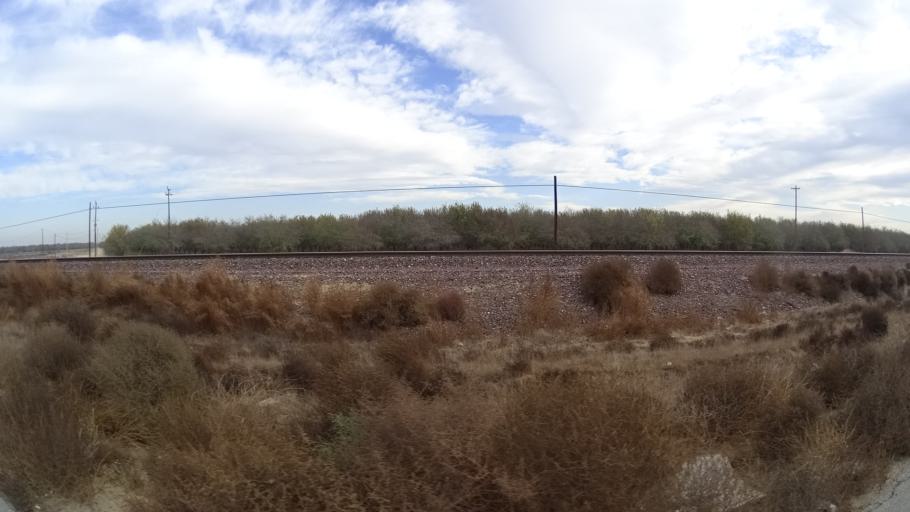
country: US
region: California
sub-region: Kern County
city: Rosedale
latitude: 35.4303
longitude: -119.1853
